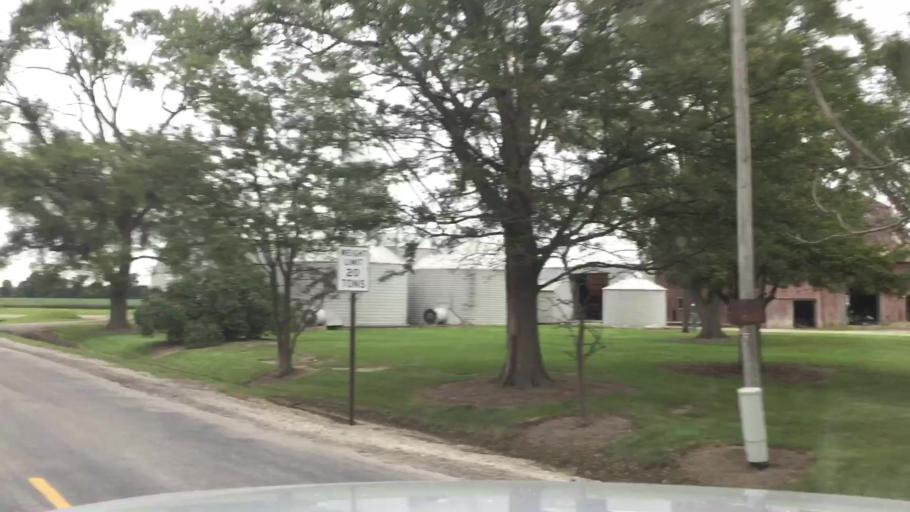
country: US
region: Michigan
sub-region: Washtenaw County
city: Milan
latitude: 42.0758
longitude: -83.7356
